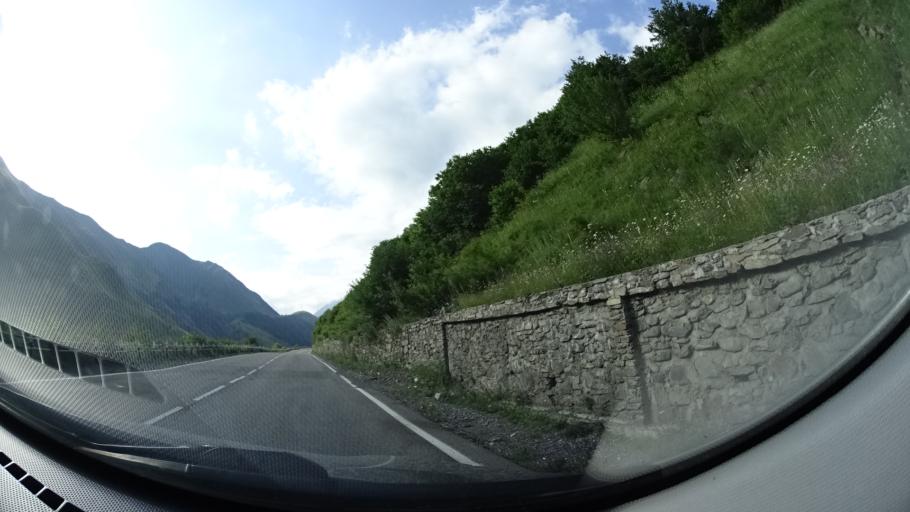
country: GE
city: Gudauri
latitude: 42.4402
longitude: 44.4845
